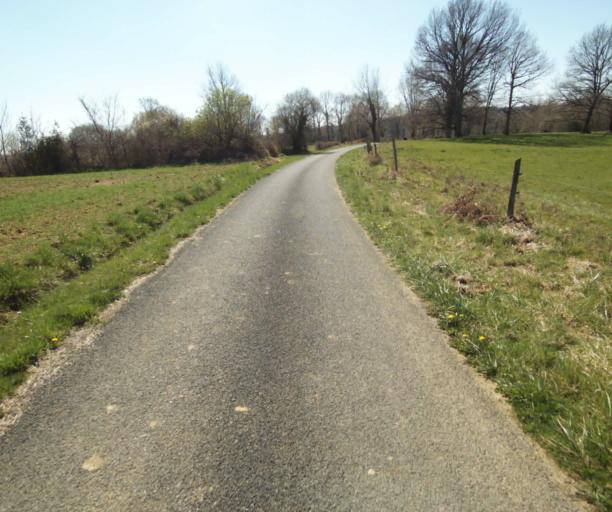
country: FR
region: Limousin
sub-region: Departement de la Correze
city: Saint-Clement
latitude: 45.3263
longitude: 1.6934
